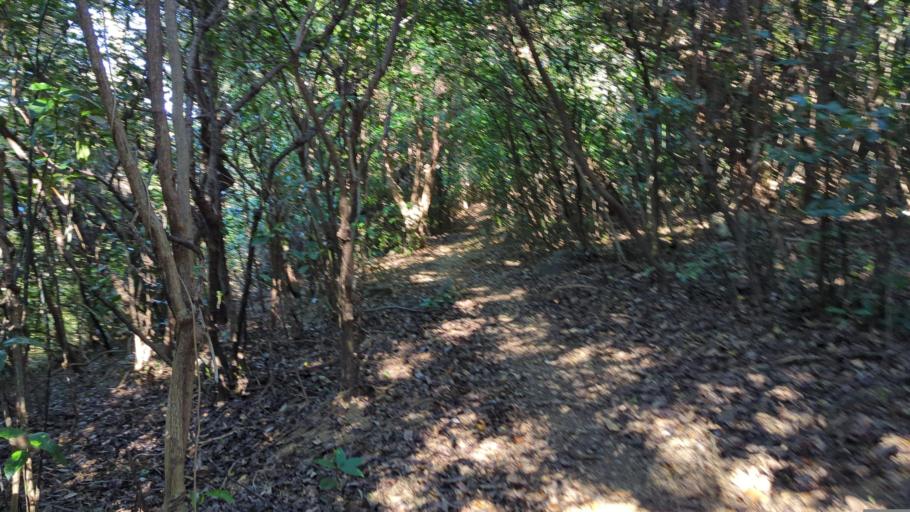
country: JP
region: Shizuoka
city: Kosai-shi
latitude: 34.7797
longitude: 137.4797
